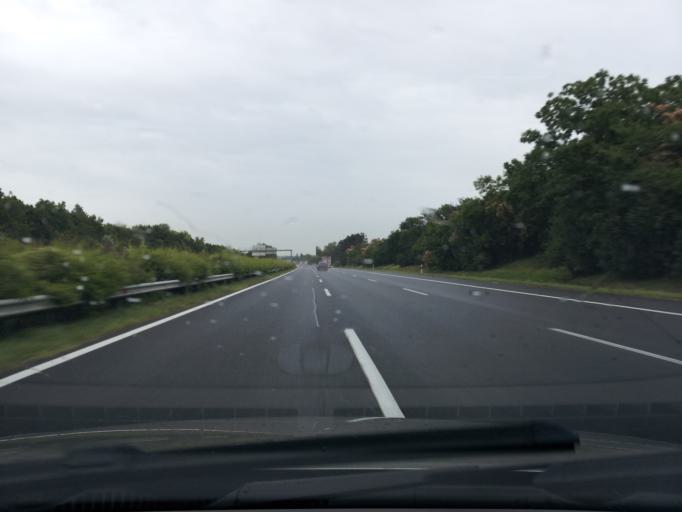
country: HU
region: Fejer
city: Szekesfehervar
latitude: 47.1518
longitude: 18.4412
